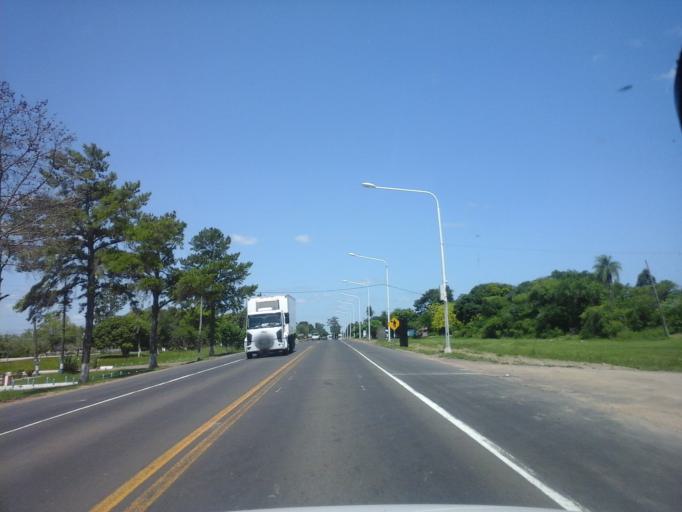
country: AR
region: Corrientes
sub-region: Departamento de Itati
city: Itati
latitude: -27.3662
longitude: -58.3005
